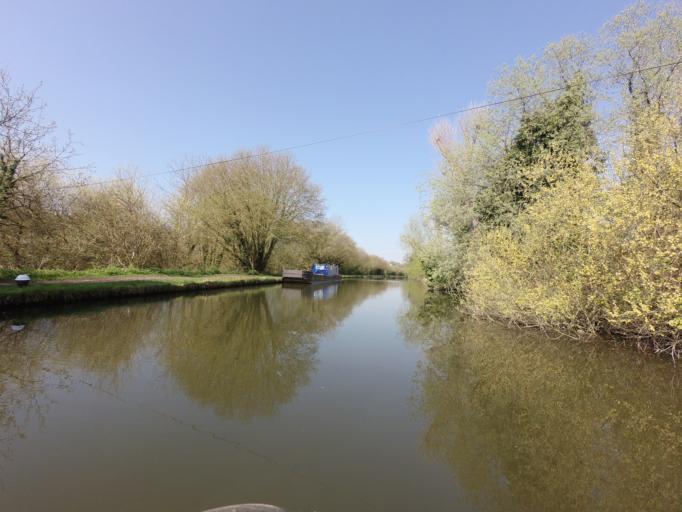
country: GB
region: England
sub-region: Hertfordshire
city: Bovingdon
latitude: 51.7509
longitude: -0.5350
